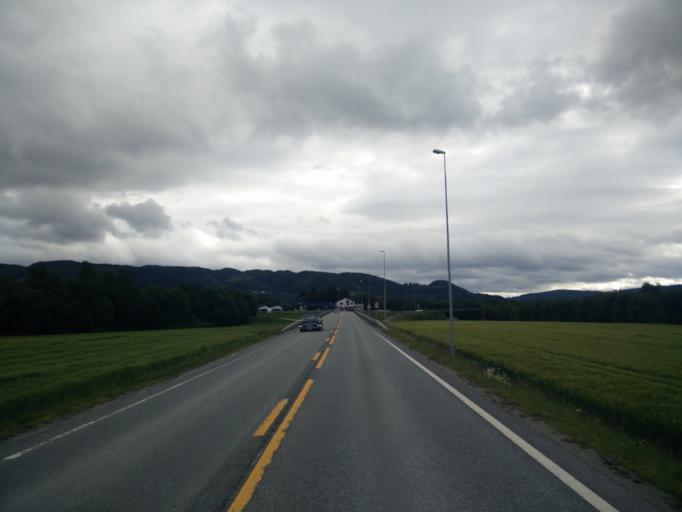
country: NO
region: Sor-Trondelag
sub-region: Orkdal
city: Orkanger
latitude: 63.2688
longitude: 9.8039
